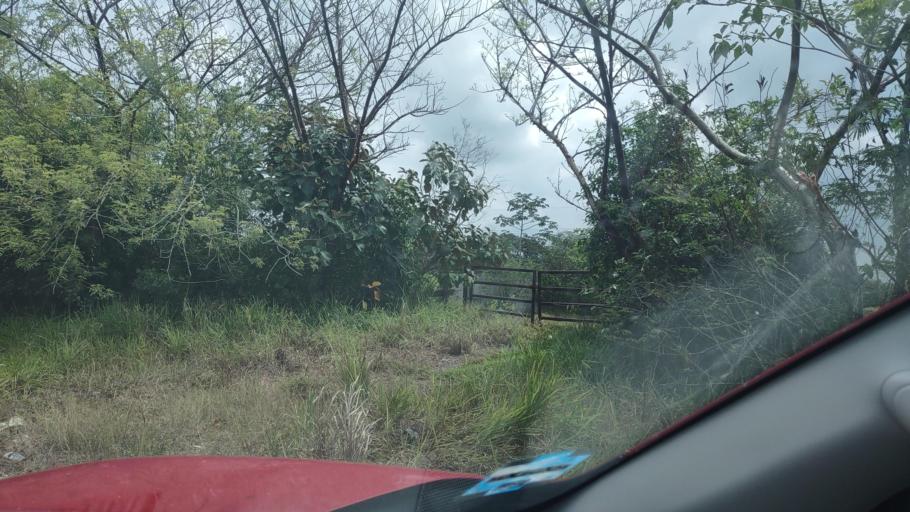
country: MX
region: Veracruz
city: Las Choapas
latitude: 17.9578
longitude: -94.1106
